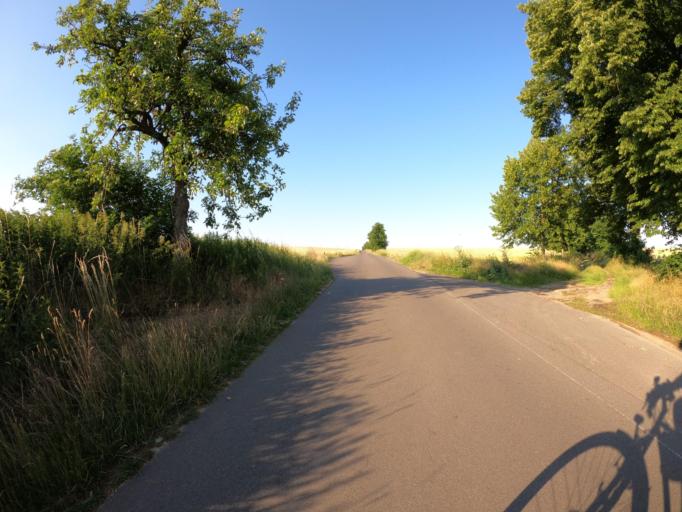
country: DE
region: Brandenburg
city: Tantow
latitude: 53.2777
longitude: 14.3570
